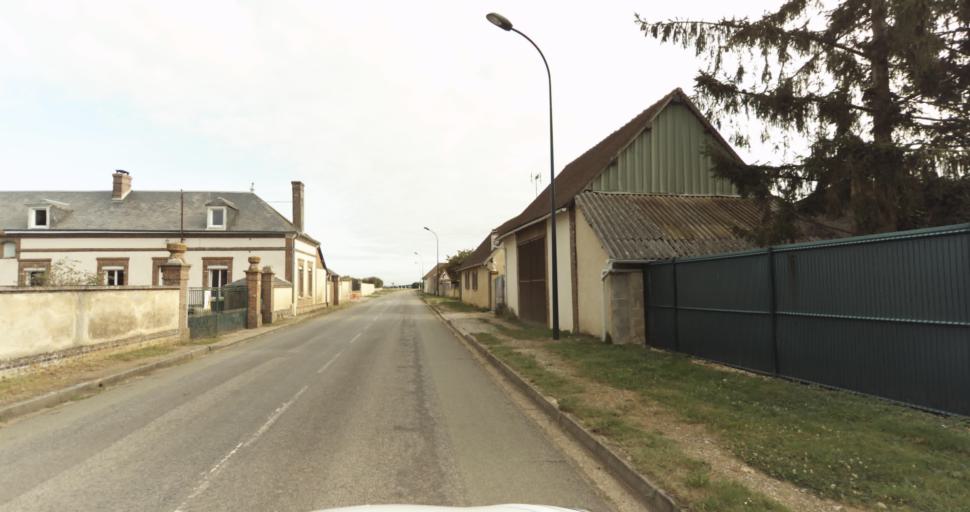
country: FR
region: Haute-Normandie
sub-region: Departement de l'Eure
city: La Madeleine-de-Nonancourt
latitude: 48.8686
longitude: 1.2475
